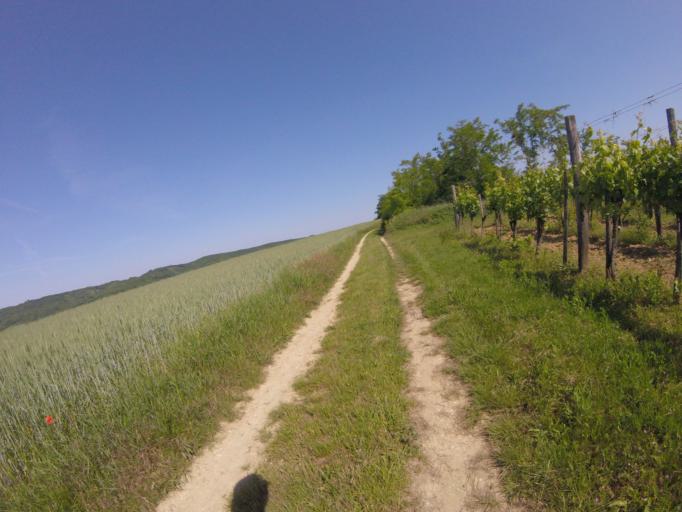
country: HU
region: Zala
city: Zalaszentgrot
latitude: 46.9014
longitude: 17.0659
